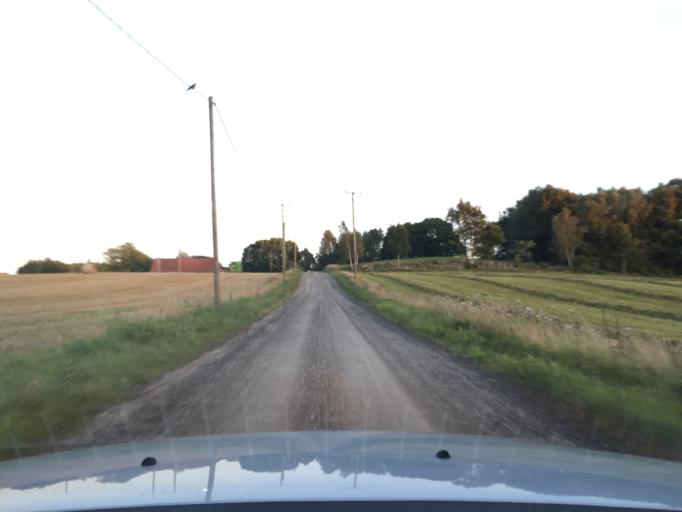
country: SE
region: Skane
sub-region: Hassleholms Kommun
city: Sosdala
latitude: 56.0071
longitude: 13.6584
